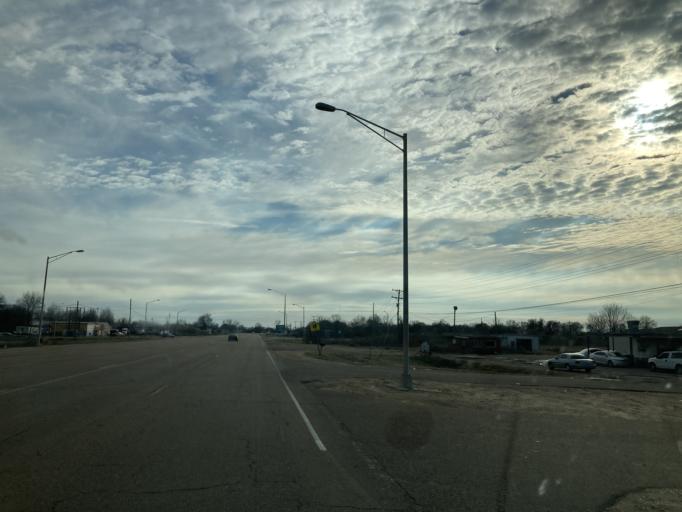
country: US
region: Mississippi
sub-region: Humphreys County
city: Belzoni
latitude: 33.1694
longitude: -90.4986
